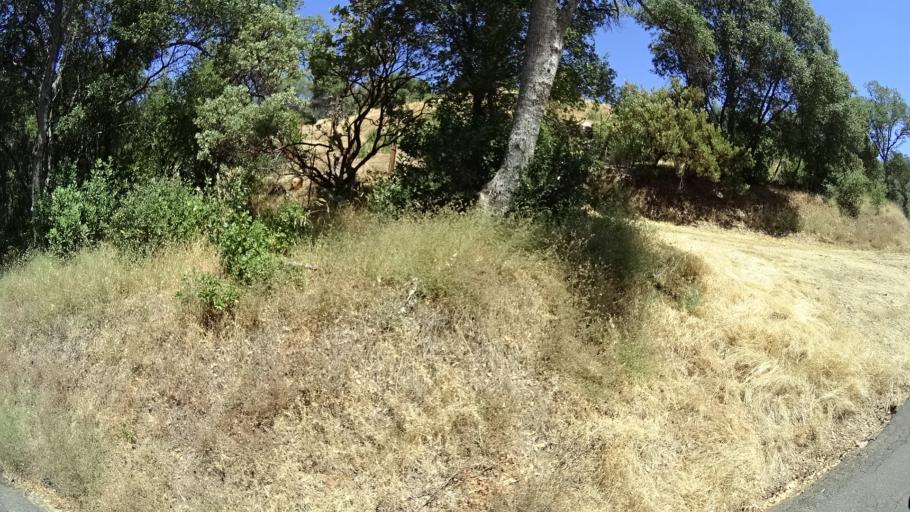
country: US
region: California
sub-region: Calaveras County
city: Forest Meadows
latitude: 38.1342
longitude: -120.4176
